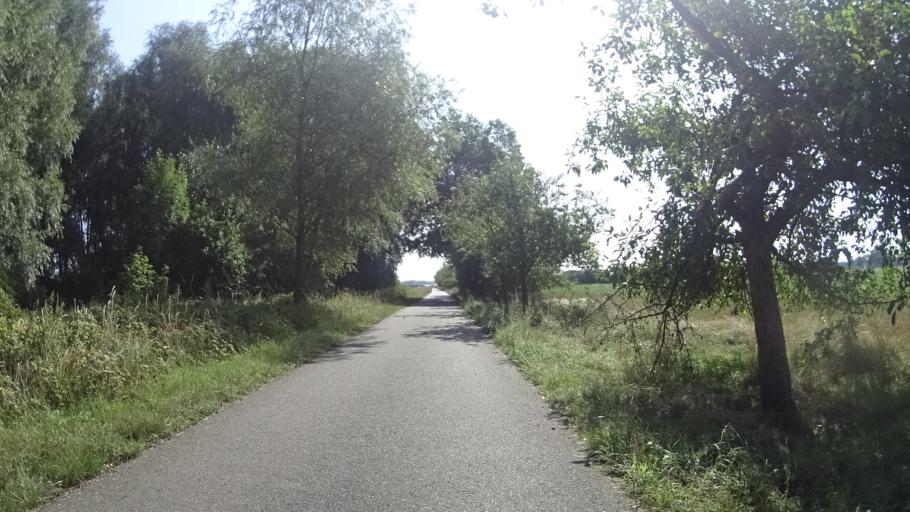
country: DE
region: Brandenburg
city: Burg
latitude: 51.8228
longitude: 14.1605
